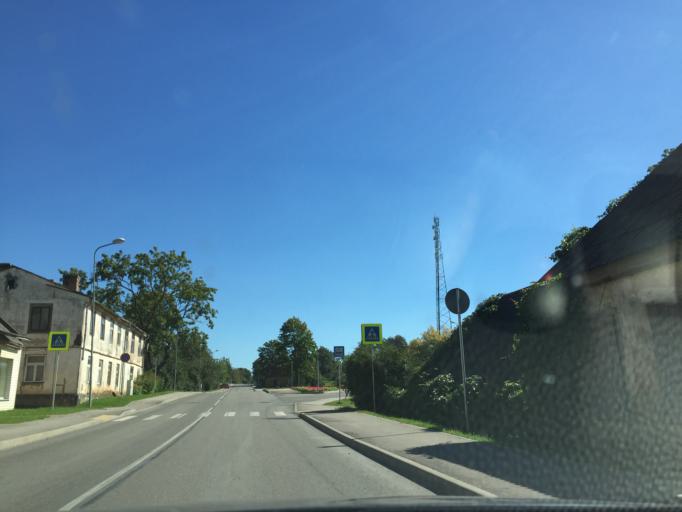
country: LV
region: Akniste
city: Akniste
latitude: 56.1614
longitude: 25.7484
